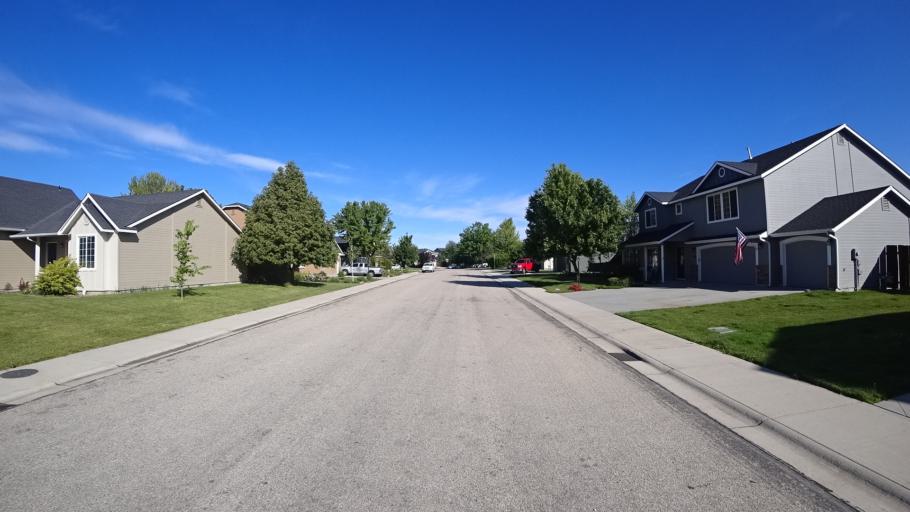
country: US
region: Idaho
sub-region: Ada County
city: Garden City
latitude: 43.5698
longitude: -116.2775
